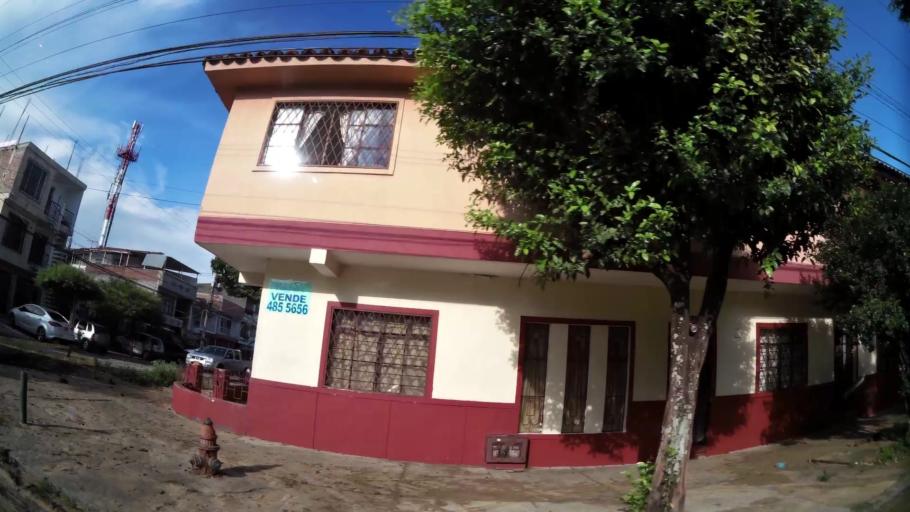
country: CO
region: Valle del Cauca
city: Cali
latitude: 3.4330
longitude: -76.5243
